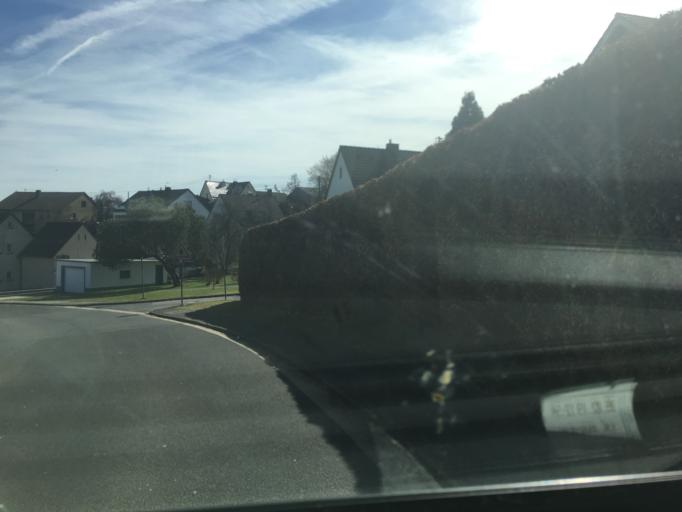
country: DE
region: North Rhine-Westphalia
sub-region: Regierungsbezirk Koln
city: Nettersheim
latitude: 50.4942
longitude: 6.6251
